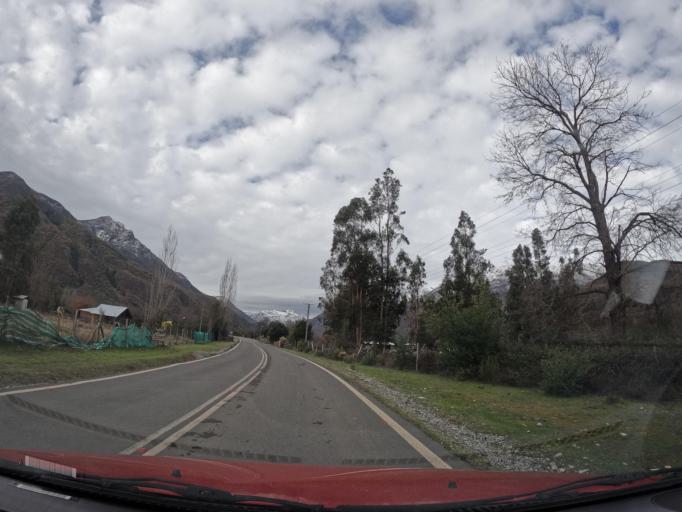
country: CL
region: Maule
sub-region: Provincia de Linares
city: Colbun
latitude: -35.8614
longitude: -71.2574
